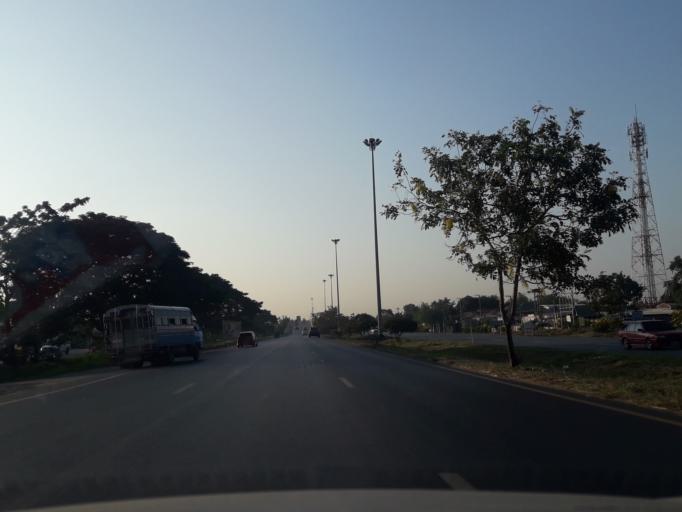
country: TH
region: Phra Nakhon Si Ayutthaya
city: Bang Pa-in
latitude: 14.1986
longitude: 100.5508
